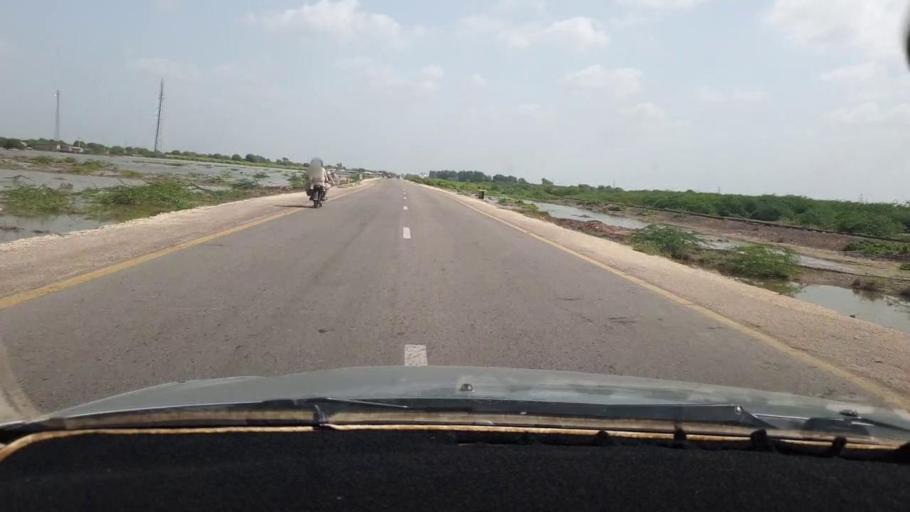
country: PK
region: Sindh
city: Digri
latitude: 25.1172
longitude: 69.1542
